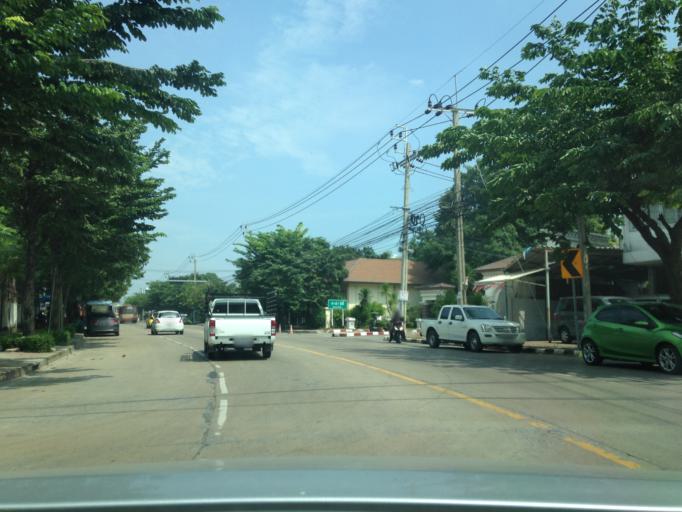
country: TH
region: Bangkok
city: Lat Phrao
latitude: 13.8328
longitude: 100.6256
